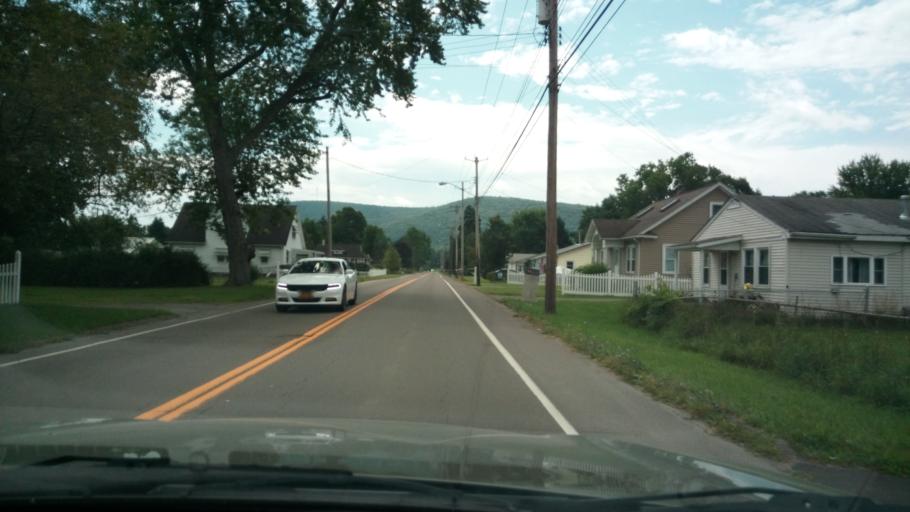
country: US
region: New York
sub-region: Chemung County
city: Southport
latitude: 42.0623
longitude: -76.7946
